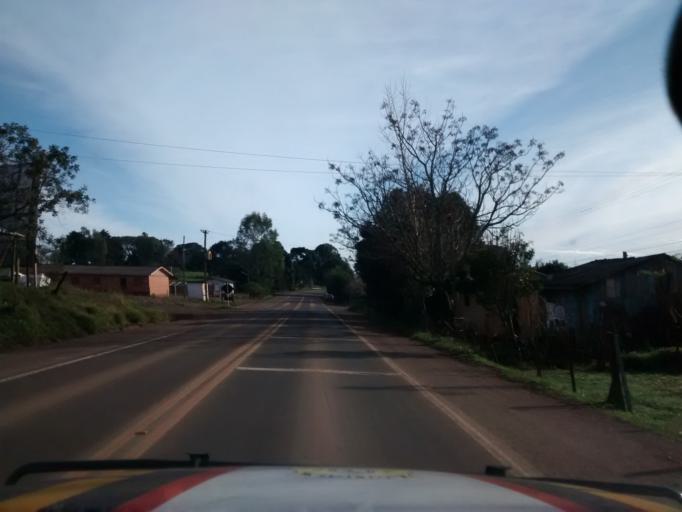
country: BR
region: Rio Grande do Sul
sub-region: Lagoa Vermelha
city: Lagoa Vermelha
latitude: -28.1950
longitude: -51.5251
